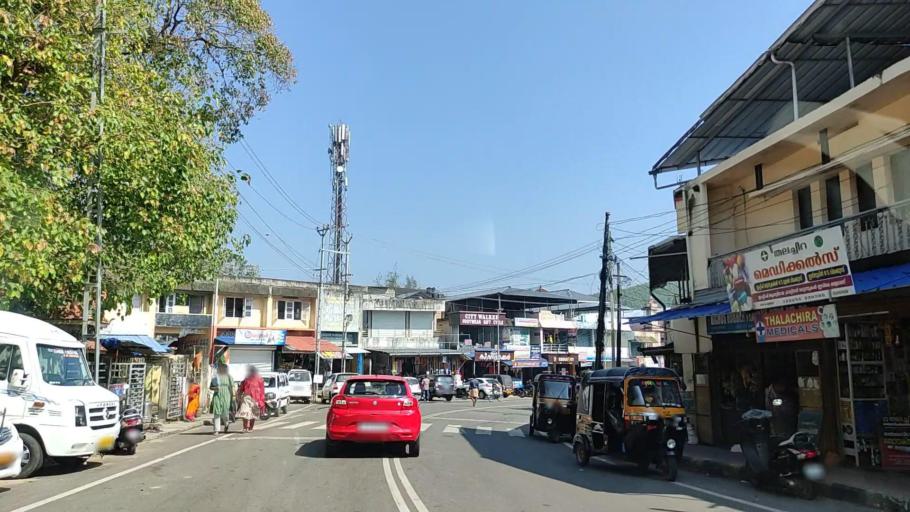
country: IN
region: Kerala
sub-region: Kollam
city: Punalur
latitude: 8.9076
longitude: 77.0548
